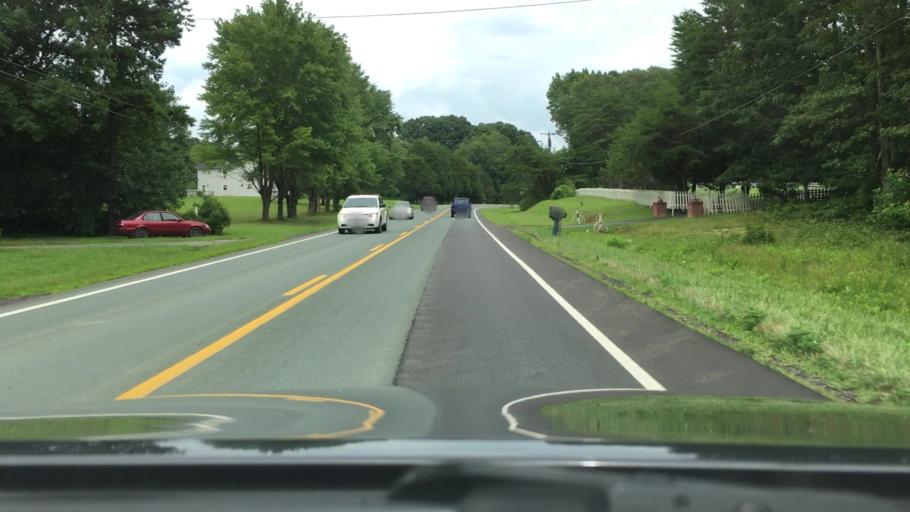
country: US
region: Virginia
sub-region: Orange County
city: Orange
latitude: 38.2581
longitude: -78.0076
